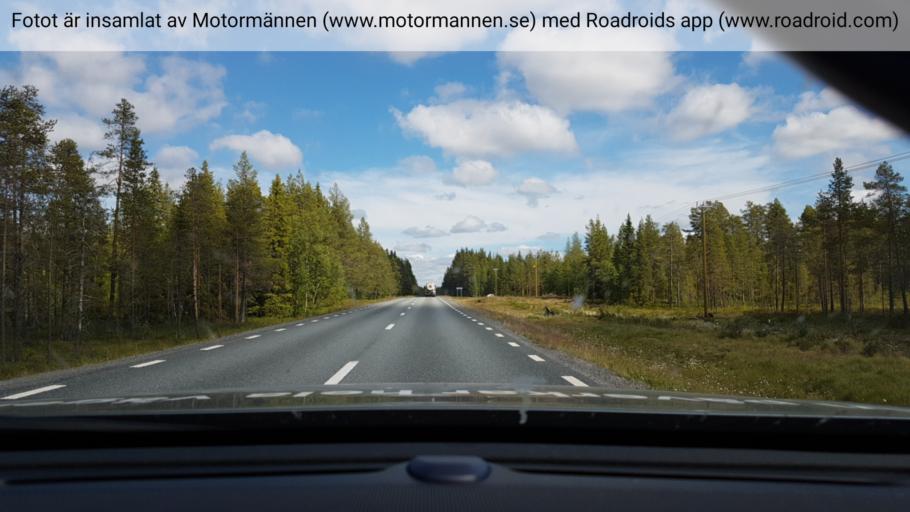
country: SE
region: Vaesterbotten
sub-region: Sorsele Kommun
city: Sorsele
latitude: 65.5592
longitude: 17.8211
